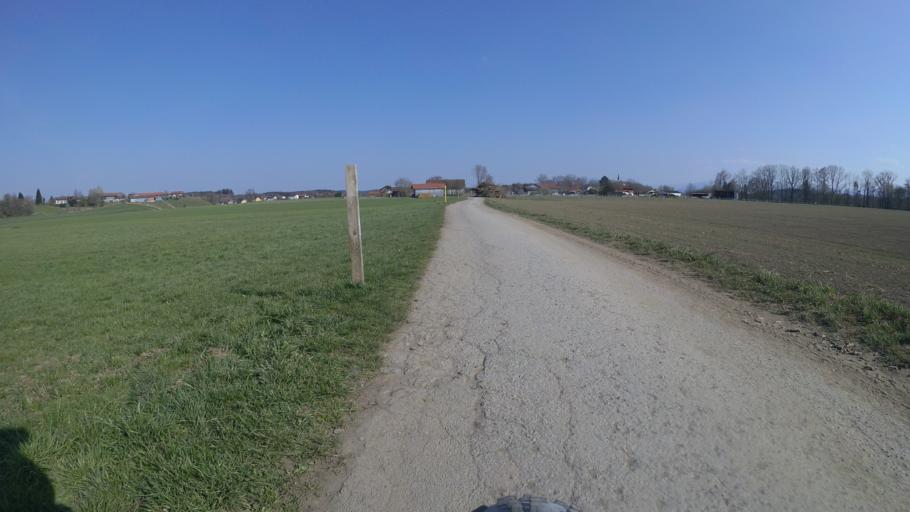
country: DE
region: Bavaria
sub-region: Upper Bavaria
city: Traunreut
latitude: 47.9487
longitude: 12.5924
